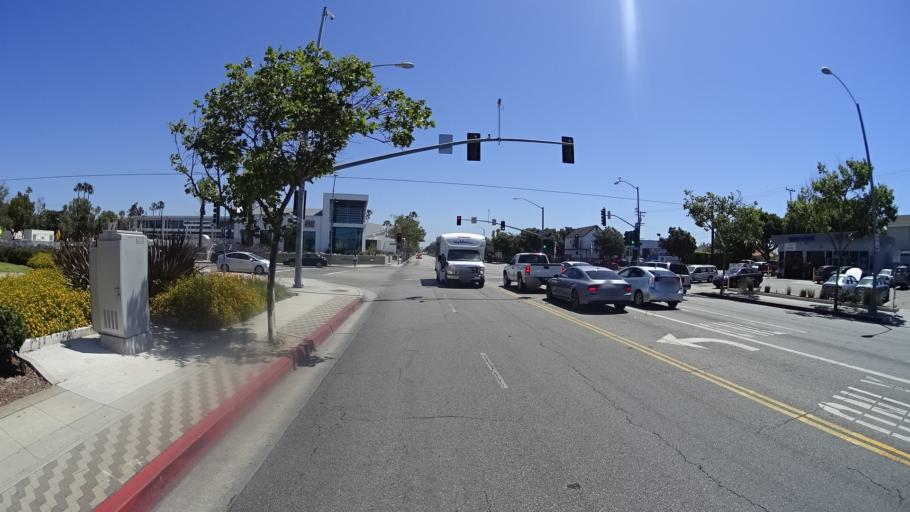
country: US
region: California
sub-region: Los Angeles County
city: Santa Monica
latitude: 34.0214
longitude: -118.4661
